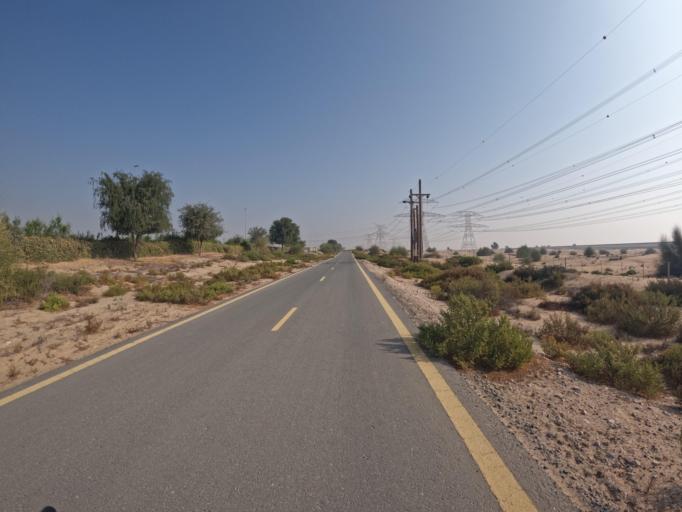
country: AE
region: Dubai
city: Dubai
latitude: 25.0303
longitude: 55.2905
